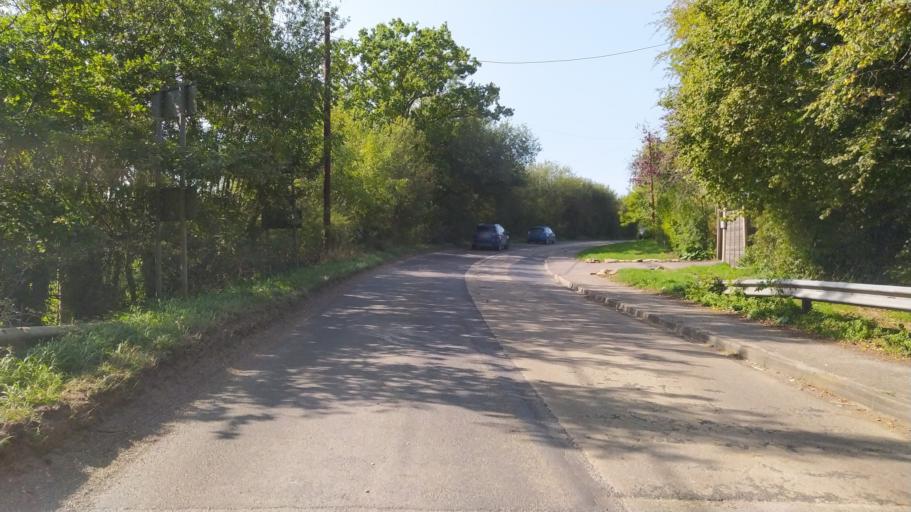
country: GB
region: England
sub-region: Hampshire
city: Hedge End
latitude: 50.9197
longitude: -1.2859
